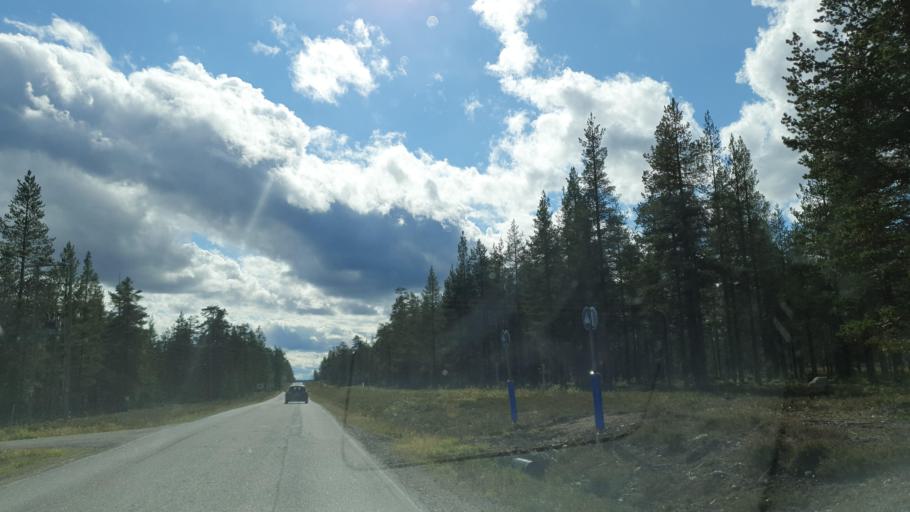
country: FI
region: Lapland
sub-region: Tunturi-Lappi
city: Kolari
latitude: 67.6476
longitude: 24.1606
